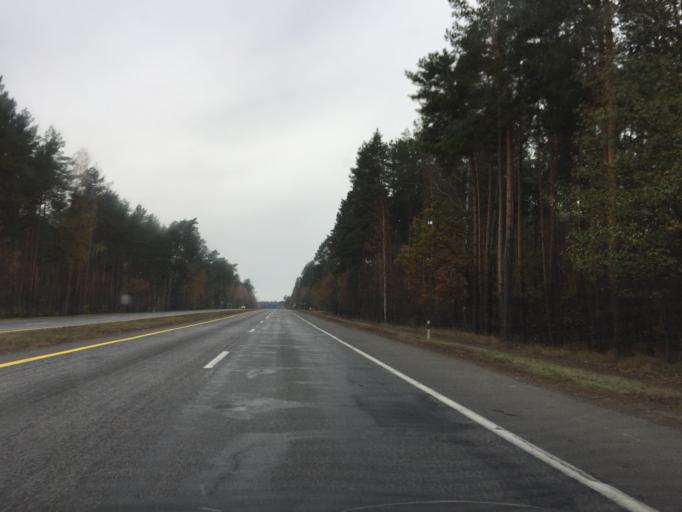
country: BY
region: Gomel
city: Horad Rechytsa
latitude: 52.3588
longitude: 30.6687
